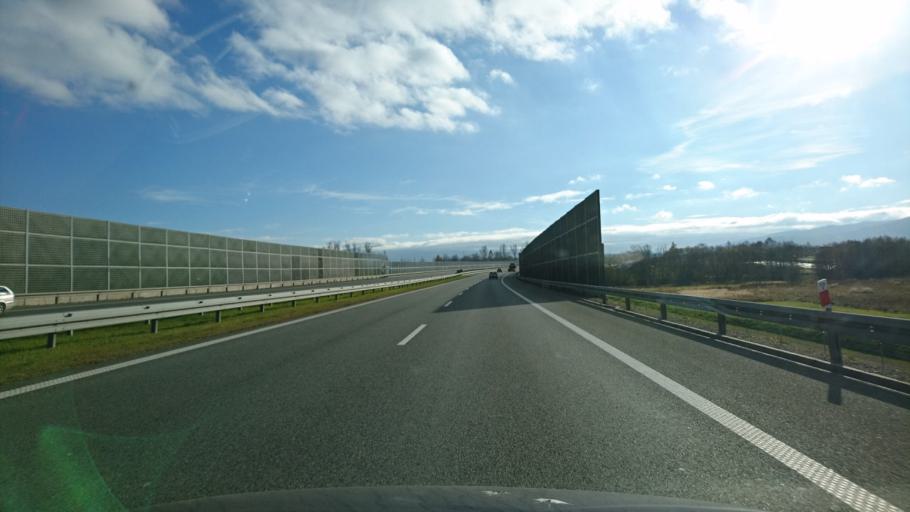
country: PL
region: Silesian Voivodeship
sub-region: Powiat zywiecki
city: Lodygowice
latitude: 49.7205
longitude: 19.1212
